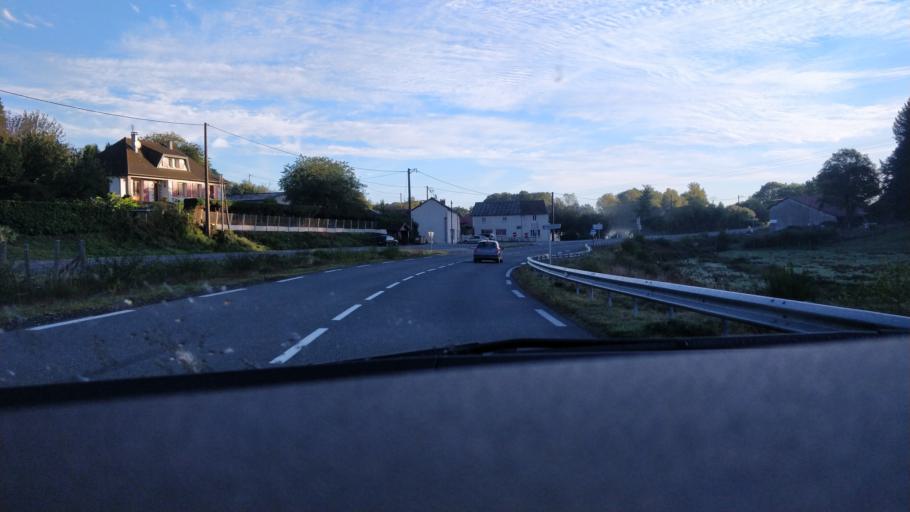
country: FR
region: Limousin
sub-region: Departement de la Creuse
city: Bourganeuf
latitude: 45.9487
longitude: 1.6841
